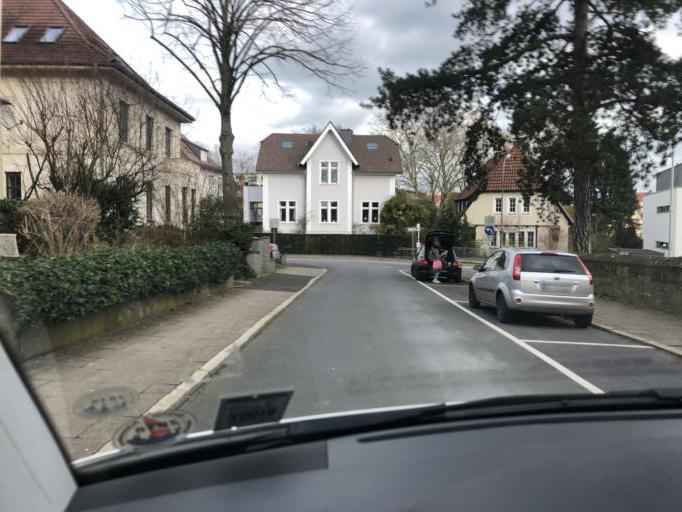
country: DE
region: North Rhine-Westphalia
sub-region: Regierungsbezirk Detmold
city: Herford
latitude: 52.1160
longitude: 8.6622
